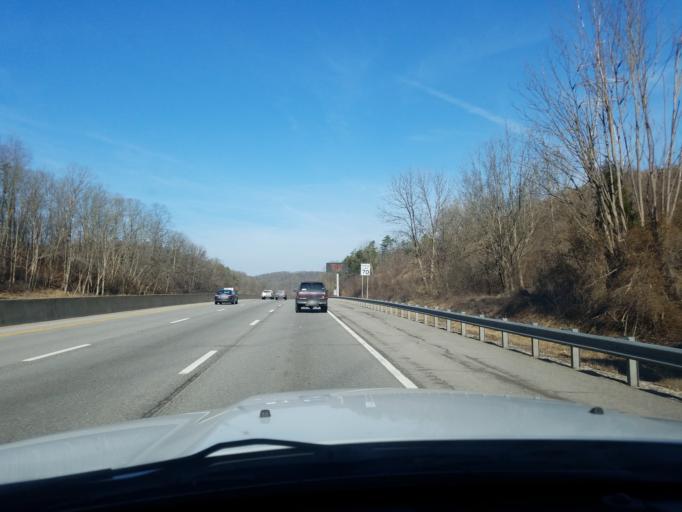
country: US
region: West Virginia
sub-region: Kanawha County
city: Cross Lanes
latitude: 38.4215
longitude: -81.8058
